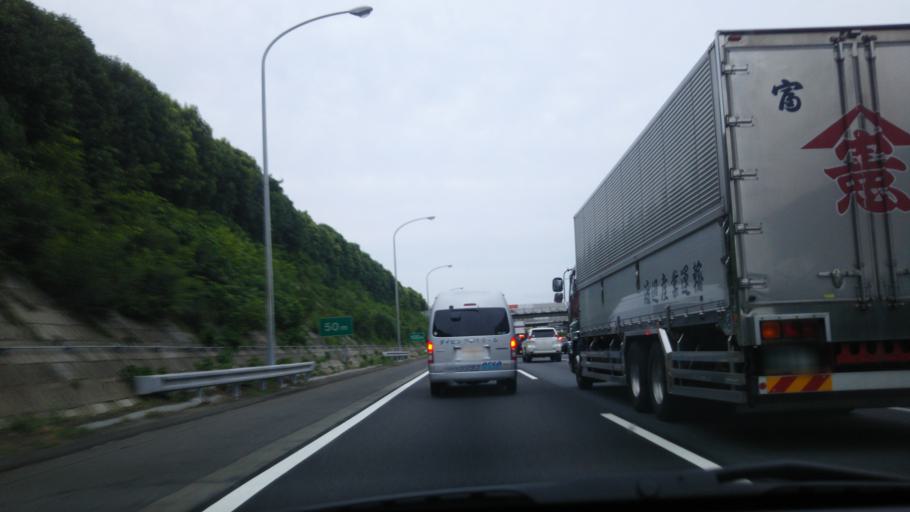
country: JP
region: Kanagawa
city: Minami-rinkan
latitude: 35.4591
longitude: 139.4304
